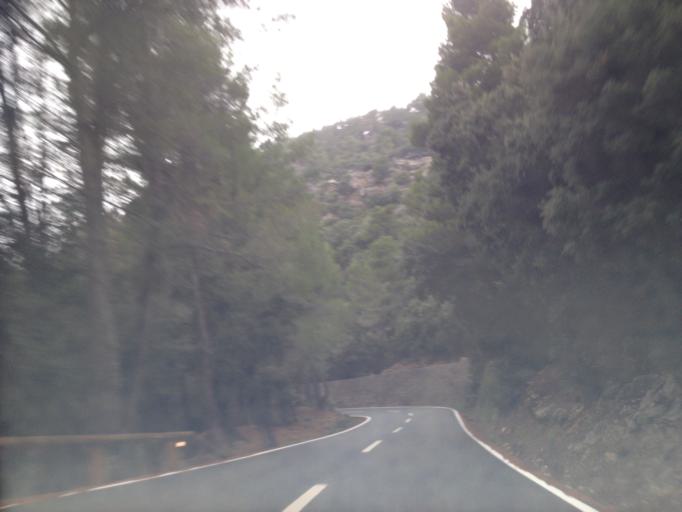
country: ES
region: Balearic Islands
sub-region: Illes Balears
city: Fornalutx
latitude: 39.7962
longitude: 2.7676
